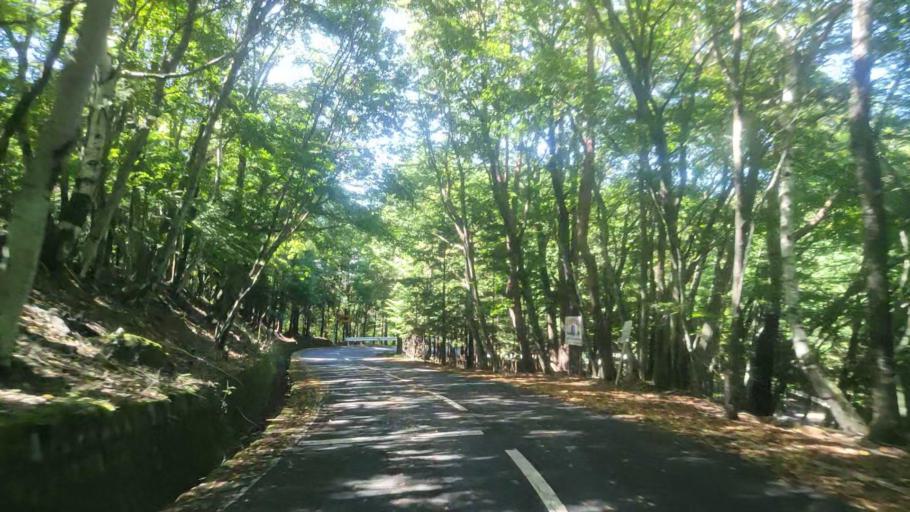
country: JP
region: Yamanashi
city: Fujikawaguchiko
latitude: 35.5715
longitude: 138.7736
